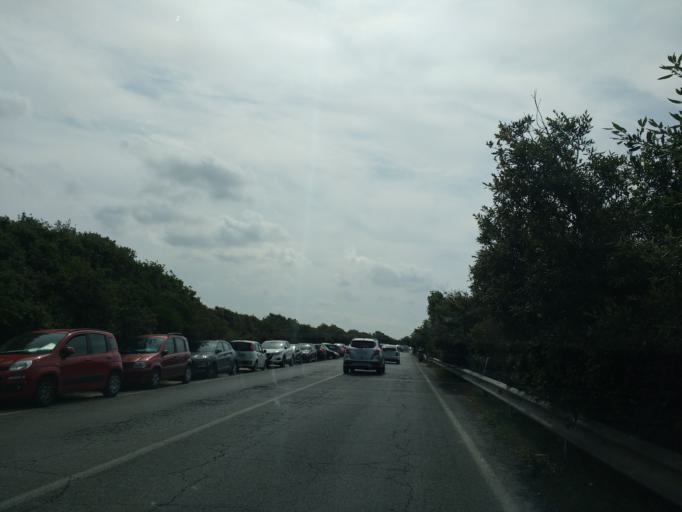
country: IT
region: Latium
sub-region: Citta metropolitana di Roma Capitale
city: Torvaianica
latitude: 41.6641
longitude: 12.4066
